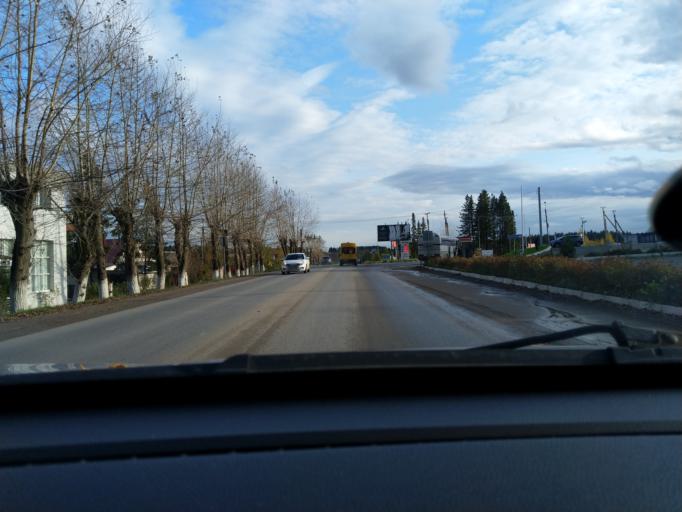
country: RU
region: Perm
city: Polazna
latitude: 58.2841
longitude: 56.4109
